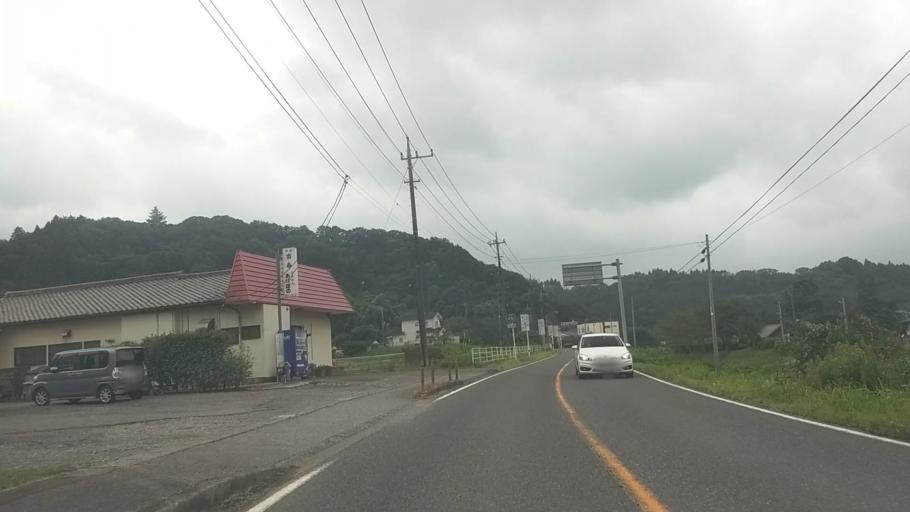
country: JP
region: Chiba
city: Kawaguchi
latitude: 35.2594
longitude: 140.0643
